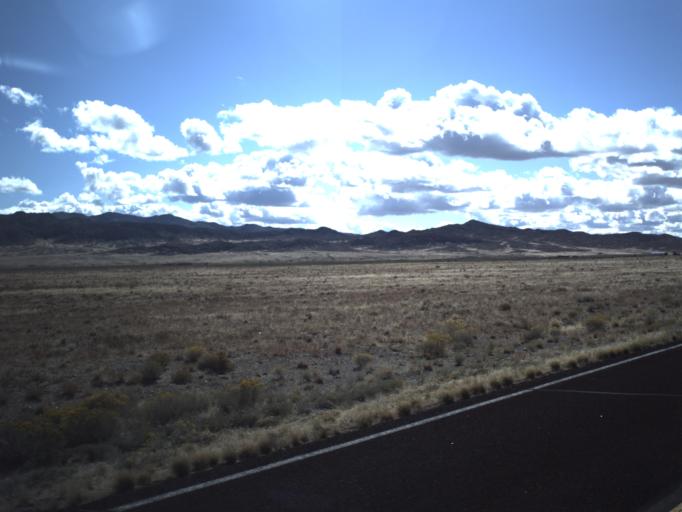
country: US
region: Nevada
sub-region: White Pine County
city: McGill
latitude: 38.9706
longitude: -114.0339
